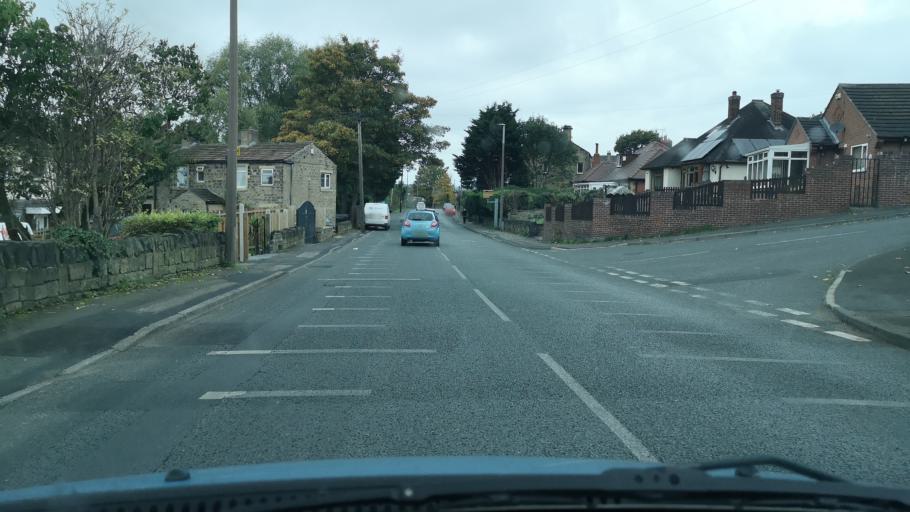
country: GB
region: England
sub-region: Kirklees
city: Heckmondwike
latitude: 53.7015
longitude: -1.6647
